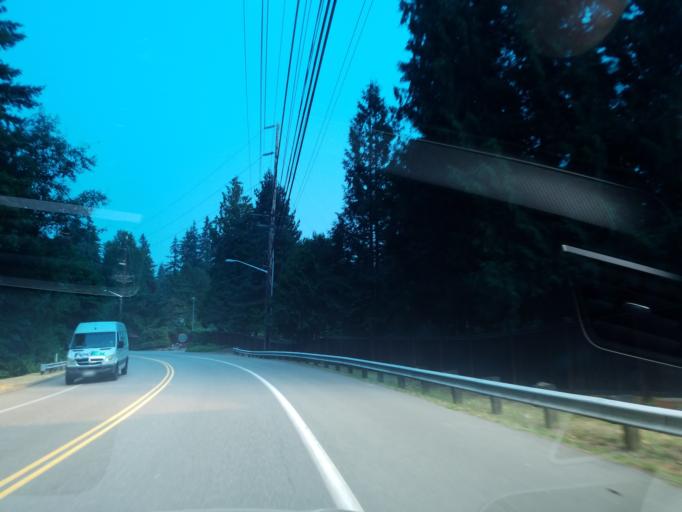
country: US
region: Washington
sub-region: King County
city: Sammamish
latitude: 47.6405
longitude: -122.0544
